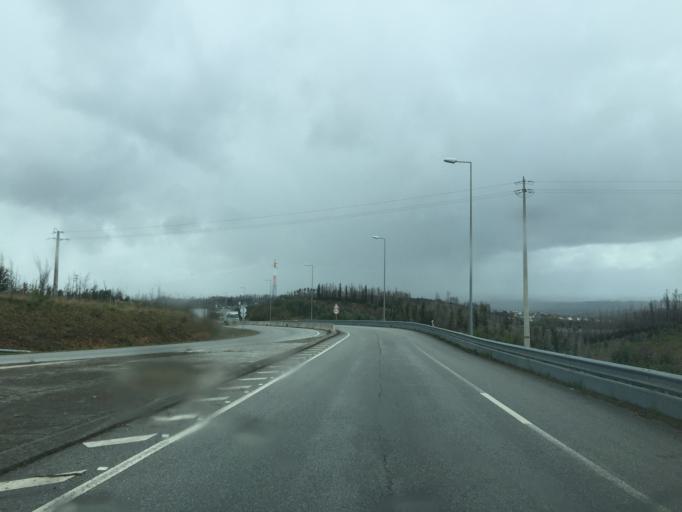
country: PT
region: Coimbra
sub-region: Tabua
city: Tabua
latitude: 40.3281
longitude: -7.9624
